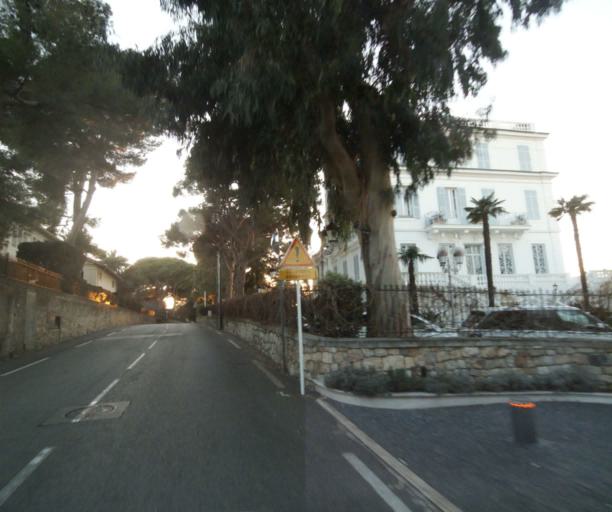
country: FR
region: Provence-Alpes-Cote d'Azur
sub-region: Departement des Alpes-Maritimes
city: Antibes
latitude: 43.5501
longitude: 7.1249
